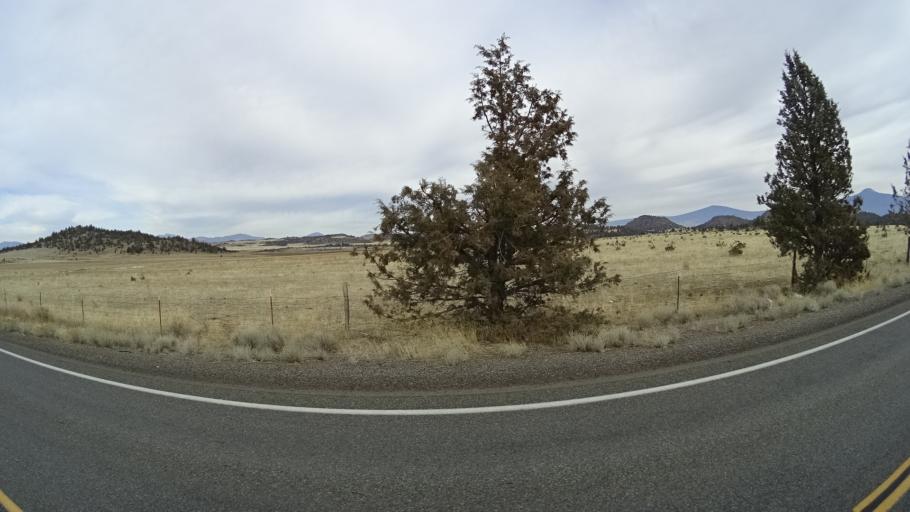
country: US
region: California
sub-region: Siskiyou County
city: Montague
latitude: 41.6402
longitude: -122.4714
